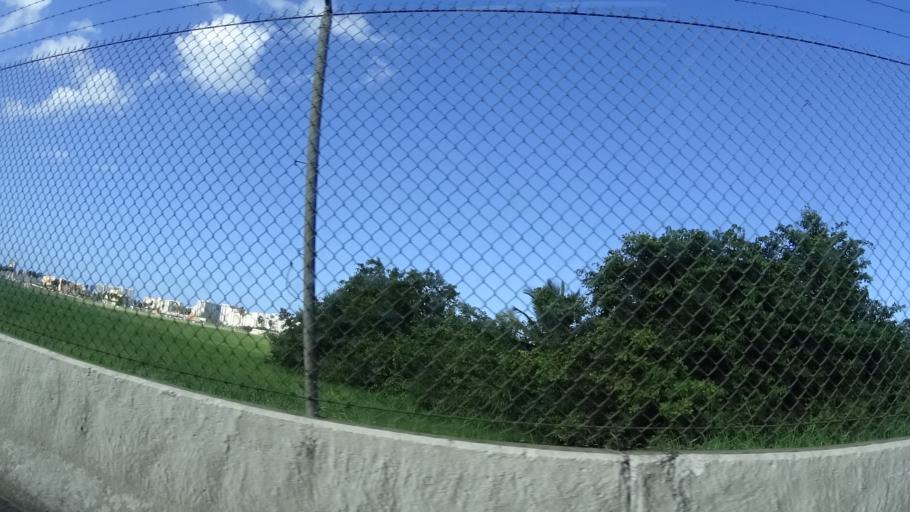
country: PR
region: Carolina
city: Carolina
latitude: 18.4323
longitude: -66.0150
